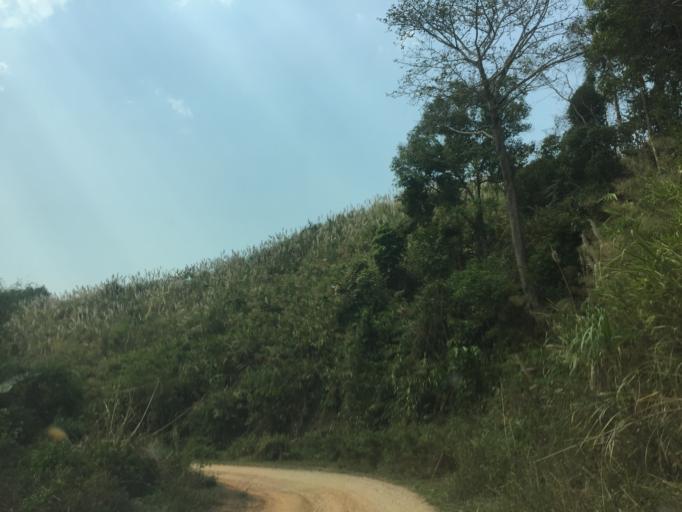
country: TH
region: Nan
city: Song Khwae
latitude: 19.7429
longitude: 100.7106
